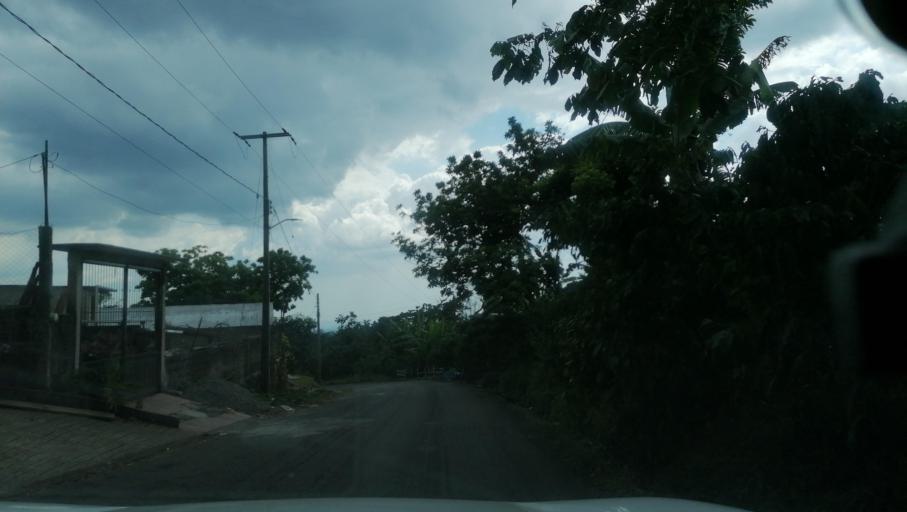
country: MX
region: Chiapas
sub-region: Cacahoatan
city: Benito Juarez
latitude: 15.0739
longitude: -92.1944
